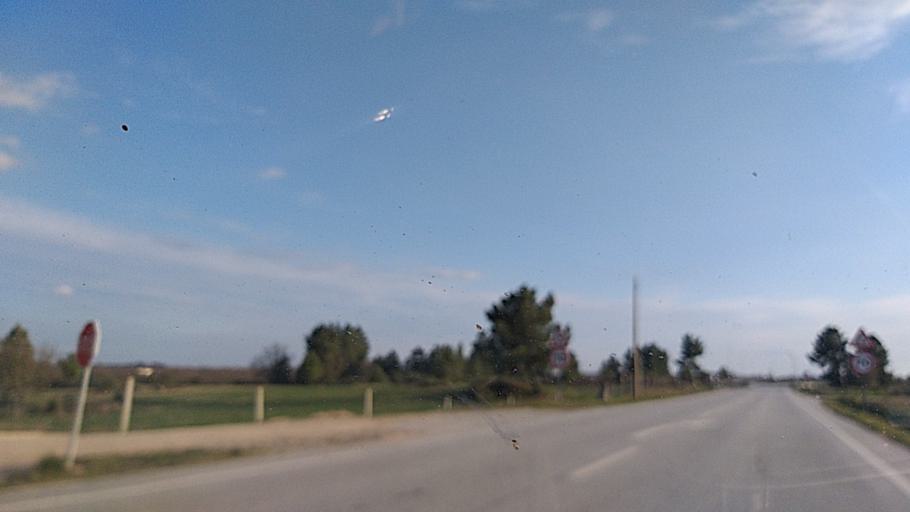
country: ES
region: Castille and Leon
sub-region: Provincia de Salamanca
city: Fuentes de Onoro
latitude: 40.6108
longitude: -6.9822
